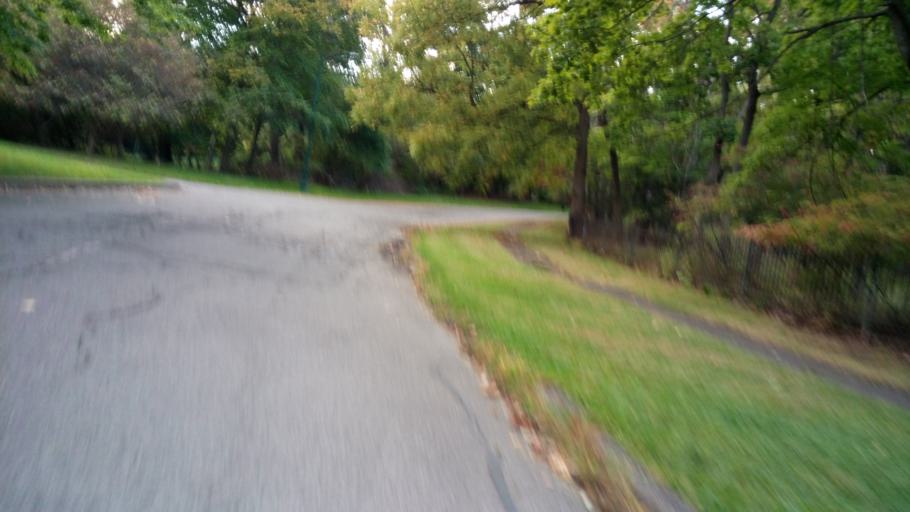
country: US
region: New York
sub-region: Chemung County
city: West Elmira
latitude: 42.0907
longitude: -76.8307
